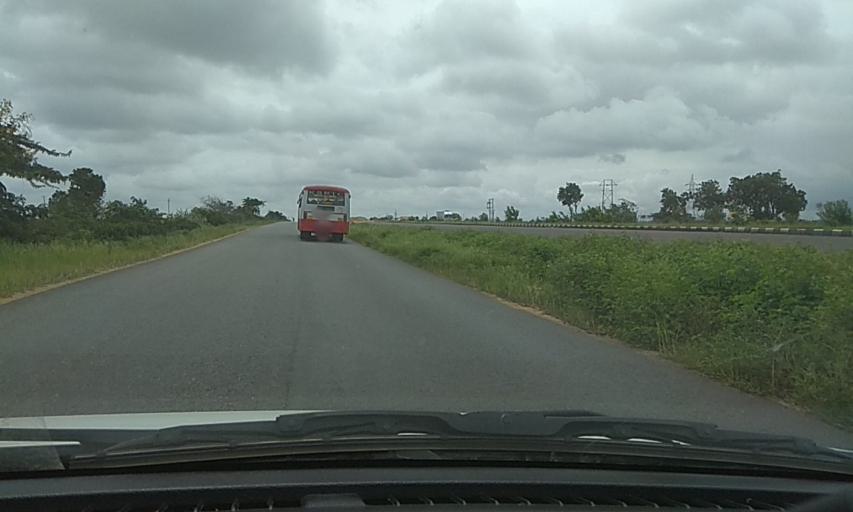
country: IN
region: Karnataka
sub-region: Chitradurga
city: Chitradurga
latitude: 14.2858
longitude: 76.2972
